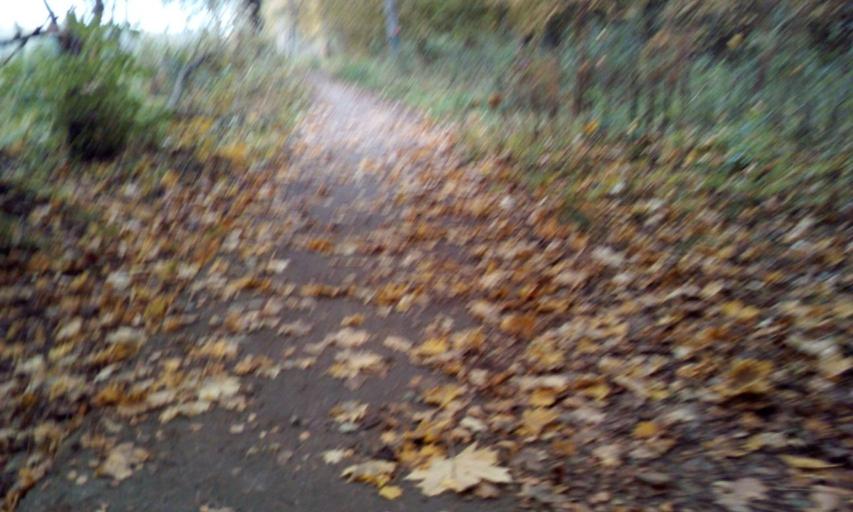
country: RU
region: Moskovskaya
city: Lesnoy Gorodok
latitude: 55.6855
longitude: 37.2190
